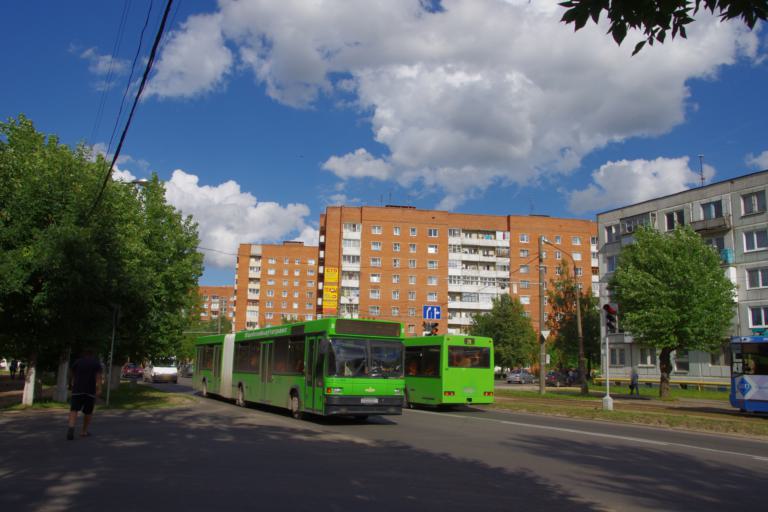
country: BY
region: Vitebsk
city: Vitebsk
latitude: 55.2103
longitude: 30.2243
